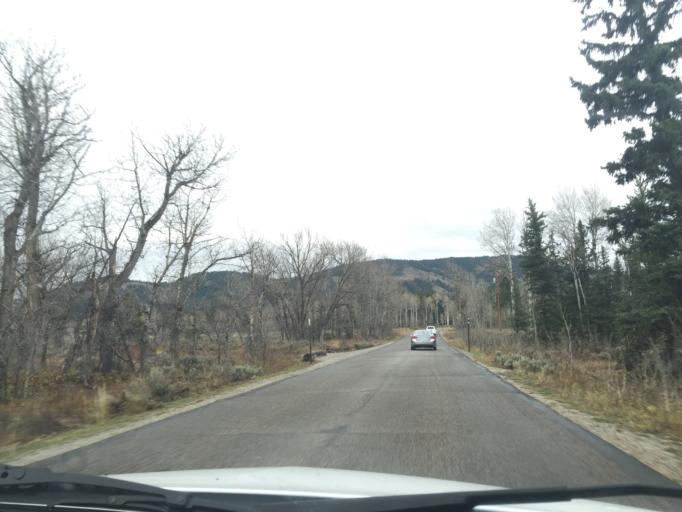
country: US
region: Wyoming
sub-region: Teton County
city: Moose Wilson Road
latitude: 43.6589
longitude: -110.7240
